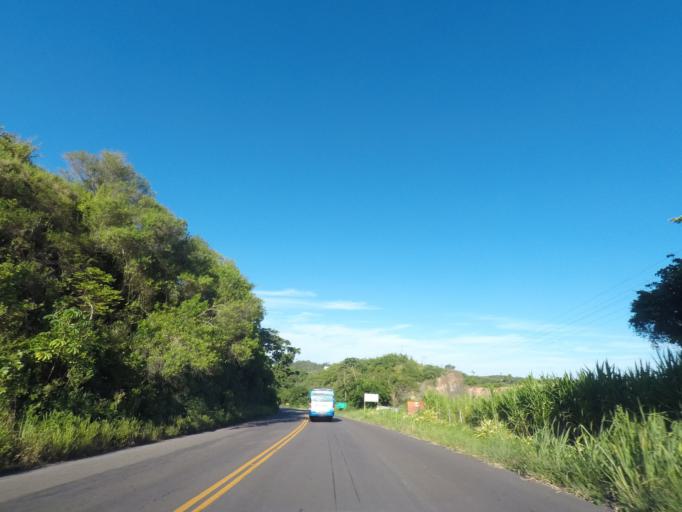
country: BR
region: Bahia
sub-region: Nazare
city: Nazare
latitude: -13.0286
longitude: -39.0033
